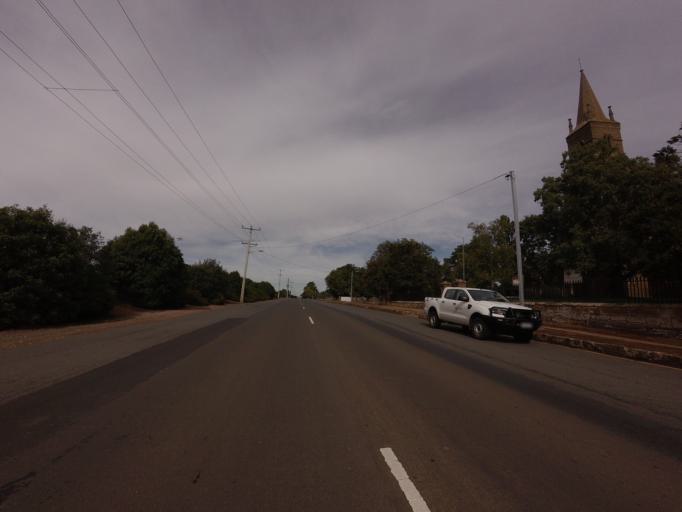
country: AU
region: Tasmania
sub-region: Brighton
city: Bridgewater
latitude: -42.3032
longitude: 147.3664
